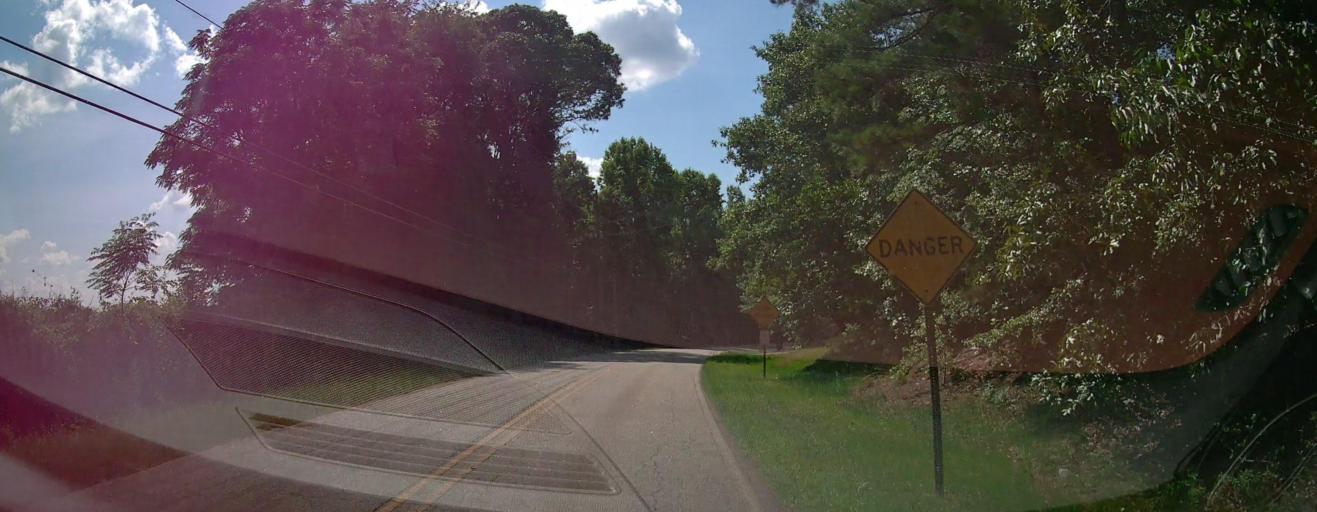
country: US
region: Georgia
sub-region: Spalding County
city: East Griffin
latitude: 33.2278
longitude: -84.1265
